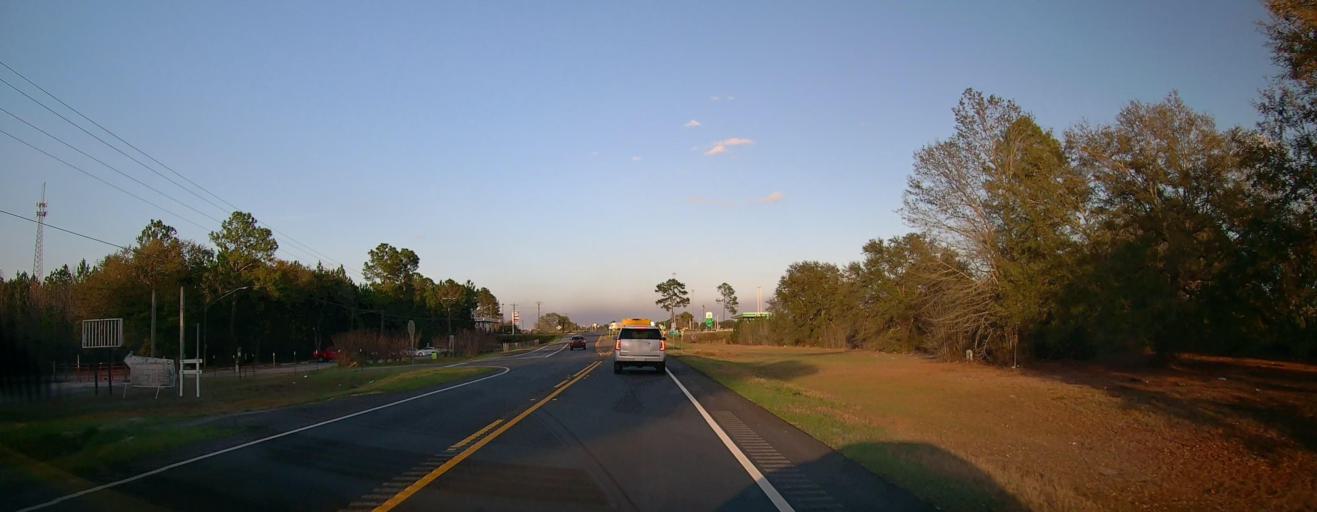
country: US
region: Georgia
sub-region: Bryan County
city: Pembroke
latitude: 32.1790
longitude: -81.4645
